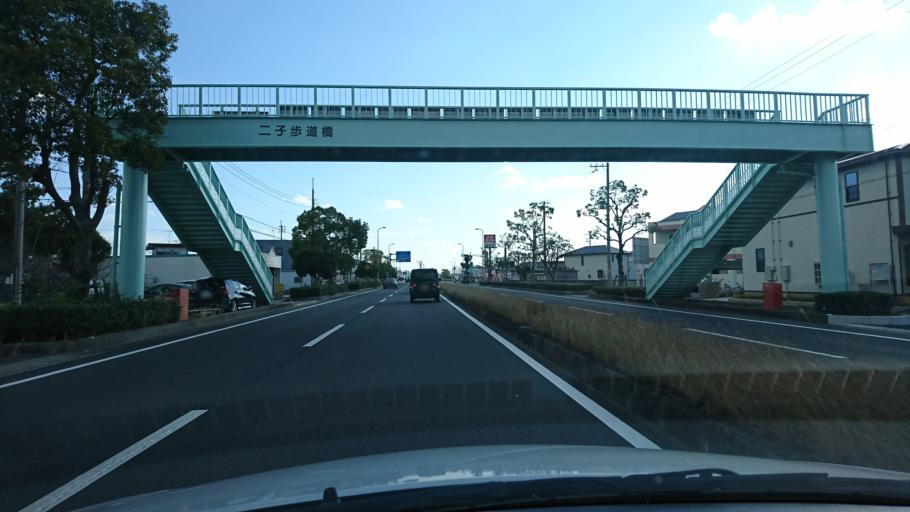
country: JP
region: Hyogo
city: Kakogawacho-honmachi
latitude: 34.7142
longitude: 134.8784
